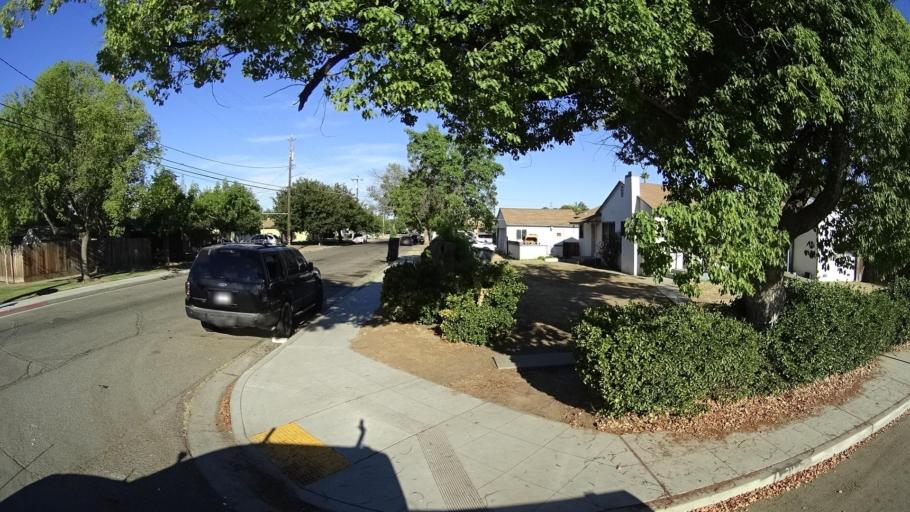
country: US
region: California
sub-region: Fresno County
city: Sunnyside
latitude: 36.7515
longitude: -119.7342
